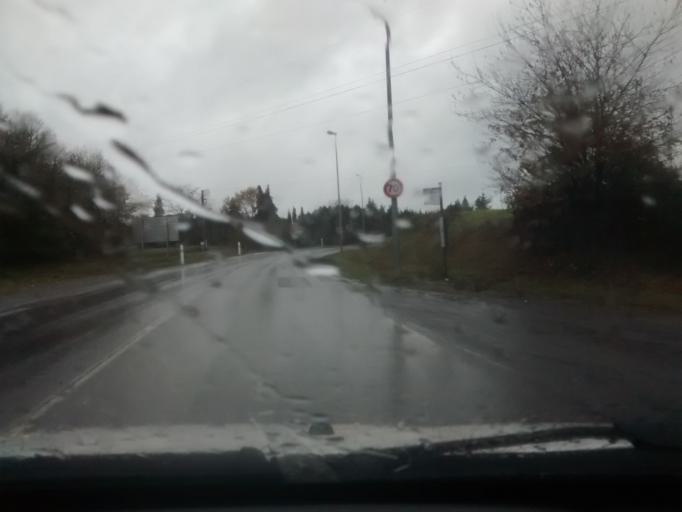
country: FR
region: Brittany
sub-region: Departement d'Ille-et-Vilaine
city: Fouillard
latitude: 48.1417
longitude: -1.5773
